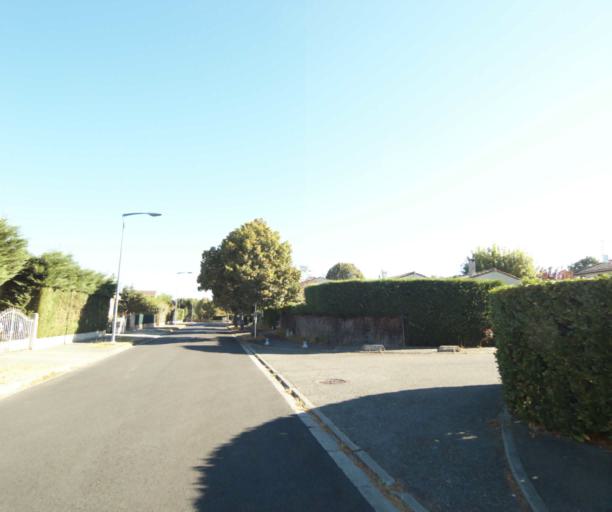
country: FR
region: Midi-Pyrenees
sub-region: Departement de la Haute-Garonne
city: Castanet-Tolosan
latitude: 43.5219
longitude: 1.5113
